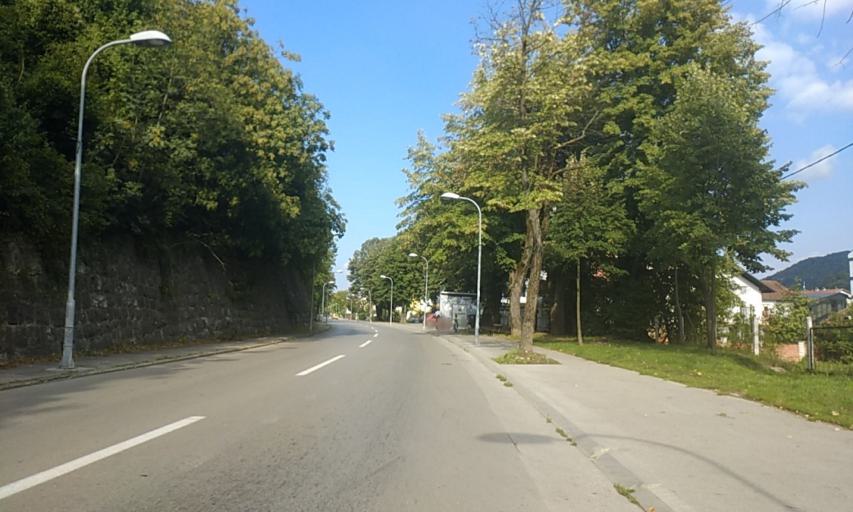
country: BA
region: Republika Srpska
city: Hiseti
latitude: 44.7544
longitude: 17.1738
